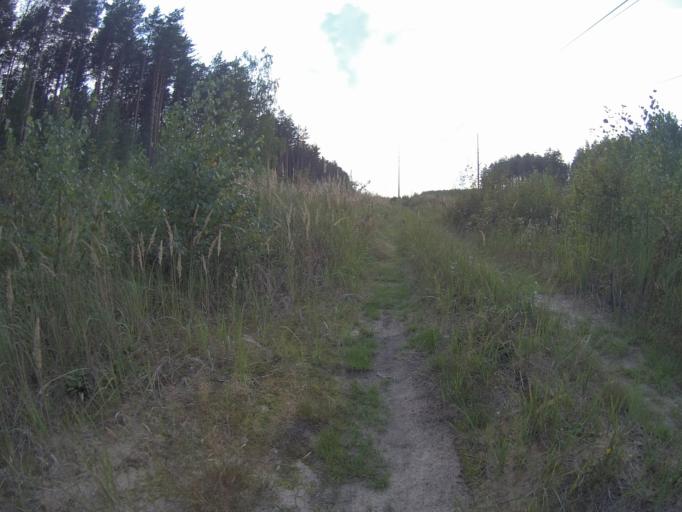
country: RU
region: Vladimir
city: Raduzhnyy
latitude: 56.0154
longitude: 40.2982
